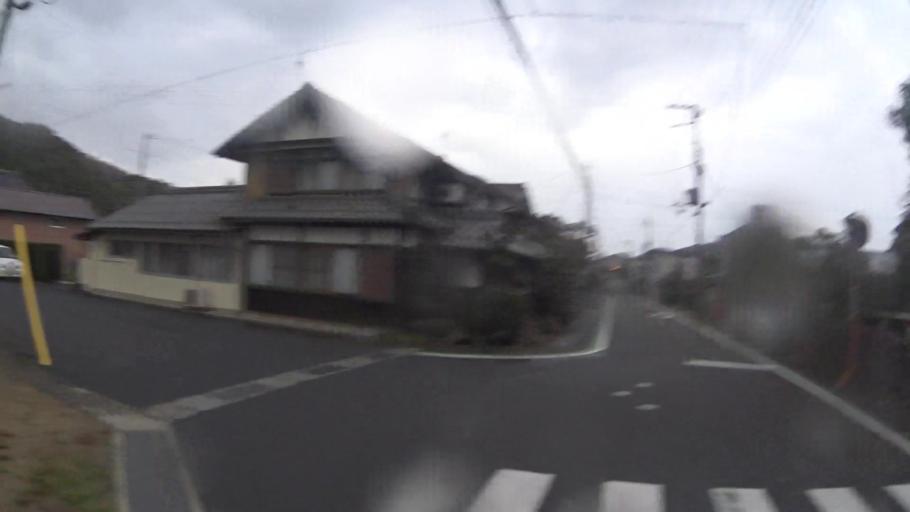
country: JP
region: Kyoto
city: Miyazu
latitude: 35.5442
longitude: 135.2367
